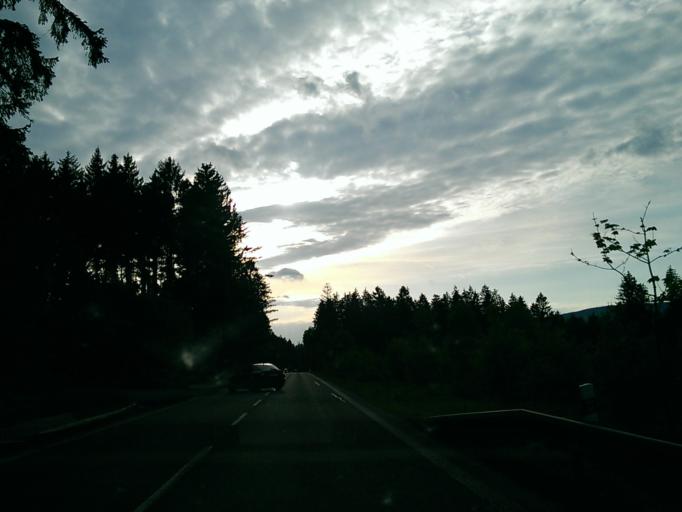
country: CZ
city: Plavy
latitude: 50.6824
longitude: 15.2866
